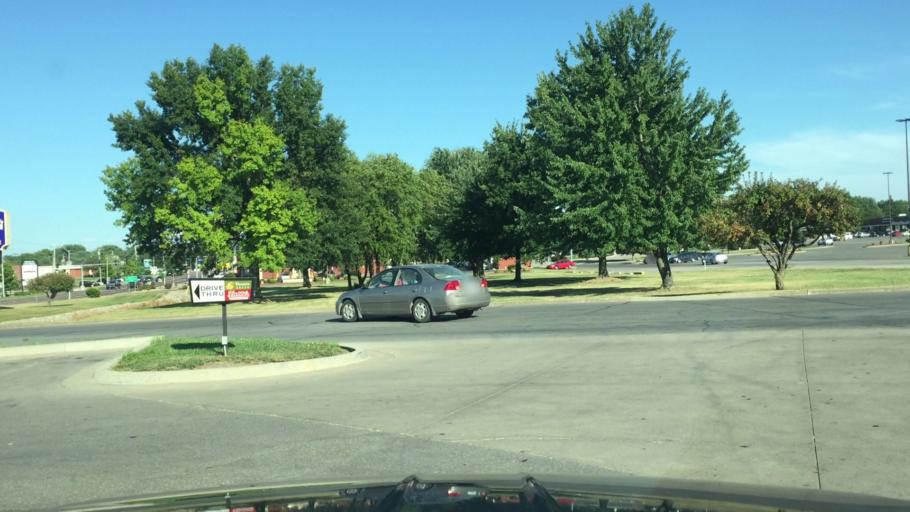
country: US
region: Missouri
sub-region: Pettis County
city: Sedalia
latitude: 38.7089
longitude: -93.2678
